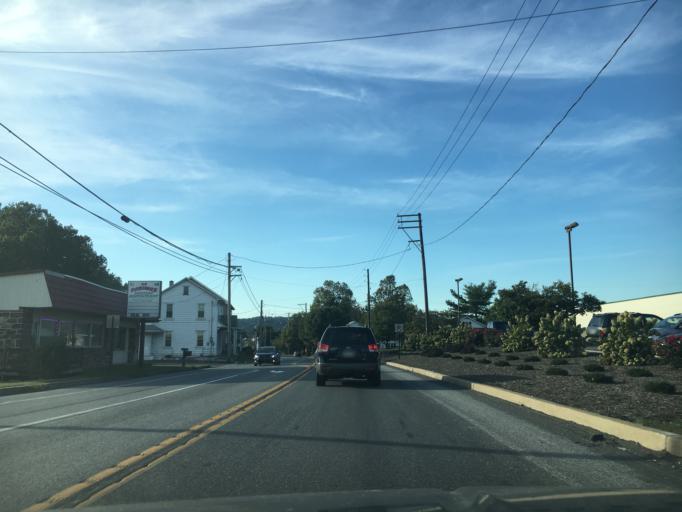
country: US
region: Pennsylvania
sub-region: Lancaster County
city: Ephrata
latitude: 40.1539
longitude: -76.1284
